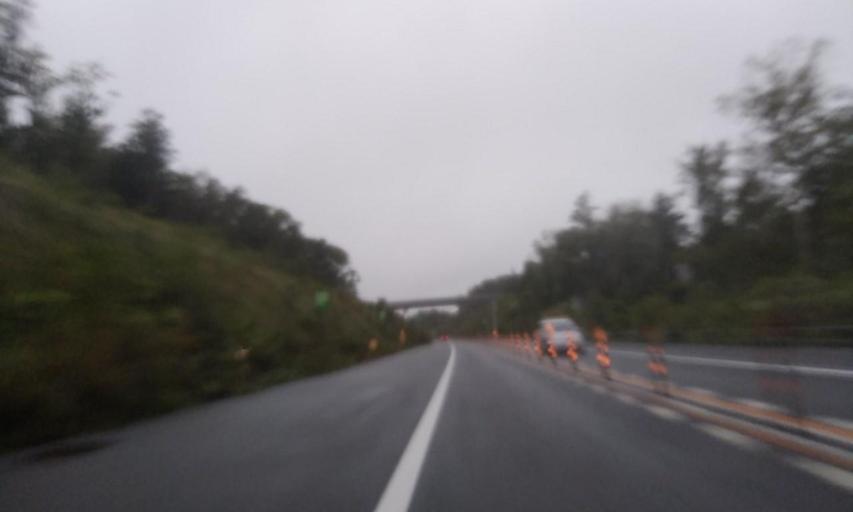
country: JP
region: Hokkaido
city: Kushiro
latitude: 43.0022
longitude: 144.4755
